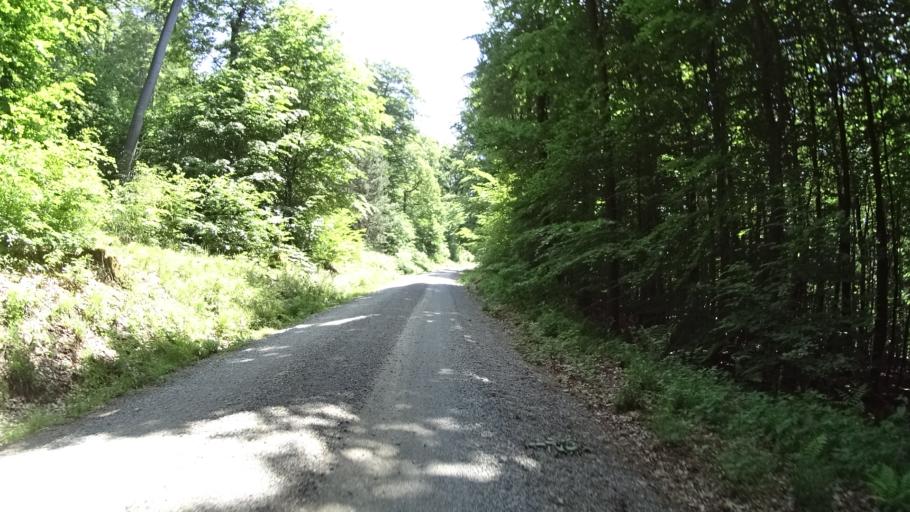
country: DE
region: Baden-Wuerttemberg
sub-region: Karlsruhe Region
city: Schonau
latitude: 49.4272
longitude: 8.7867
